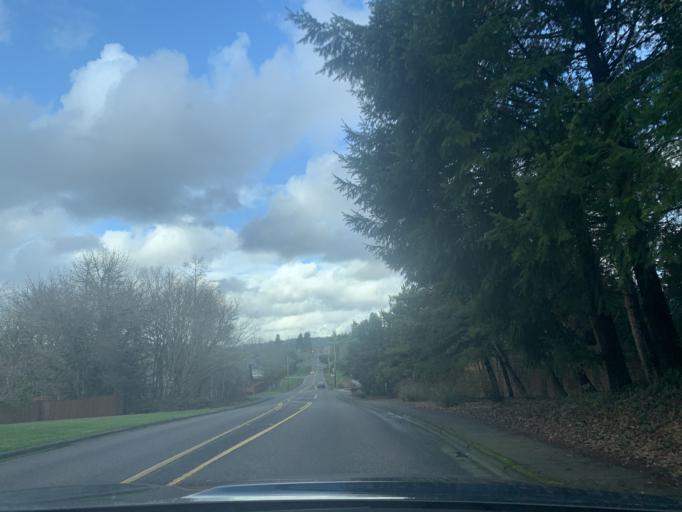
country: US
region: Oregon
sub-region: Washington County
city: Cedar Mill
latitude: 45.5436
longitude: -122.8105
